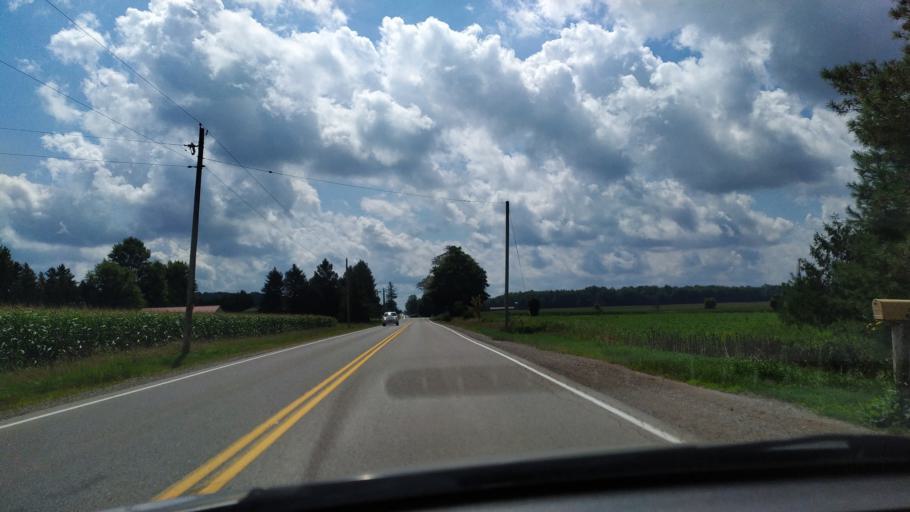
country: CA
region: Ontario
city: London
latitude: 43.0558
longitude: -81.3301
